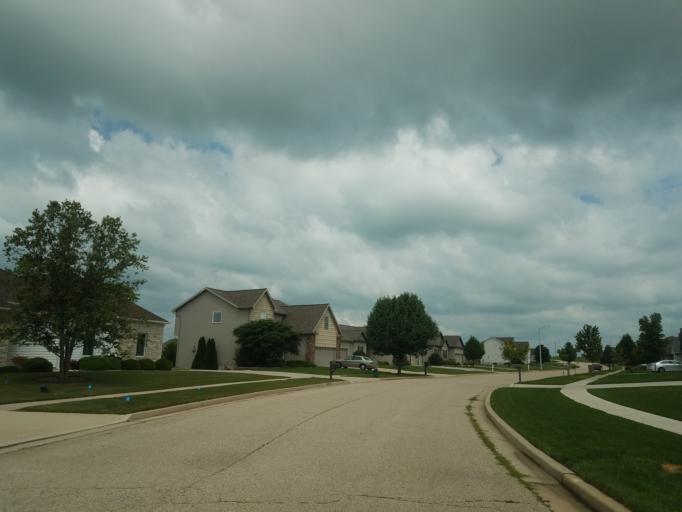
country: US
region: Illinois
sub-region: McLean County
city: Bloomington
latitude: 40.4428
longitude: -89.0380
